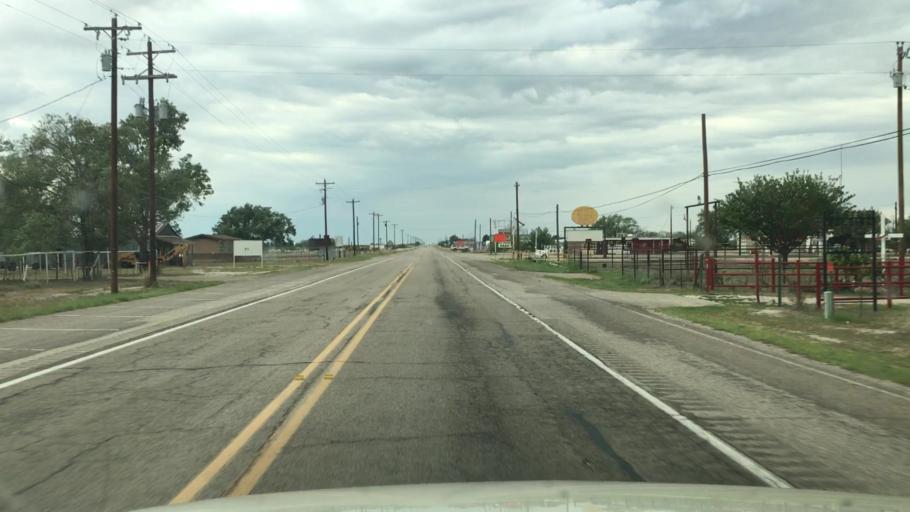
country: US
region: New Mexico
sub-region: Lea County
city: Lovington
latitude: 33.2570
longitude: -103.3381
